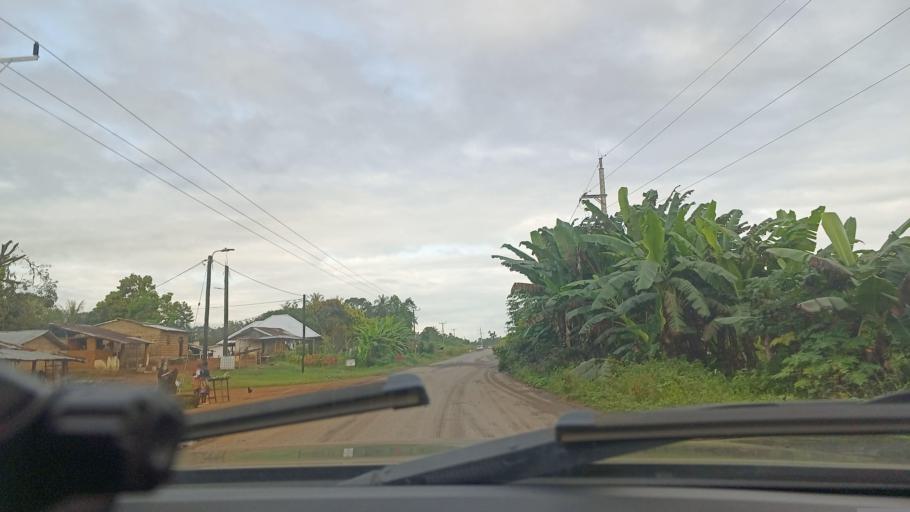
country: LR
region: Montserrado
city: Monrovia
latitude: 6.5632
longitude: -10.8724
